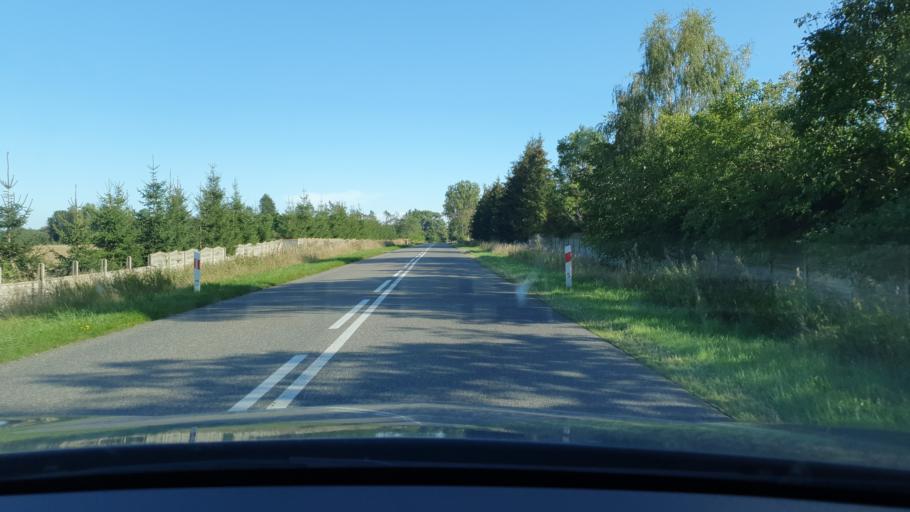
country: PL
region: West Pomeranian Voivodeship
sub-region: Powiat goleniowski
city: Przybiernow
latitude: 53.8338
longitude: 14.7676
